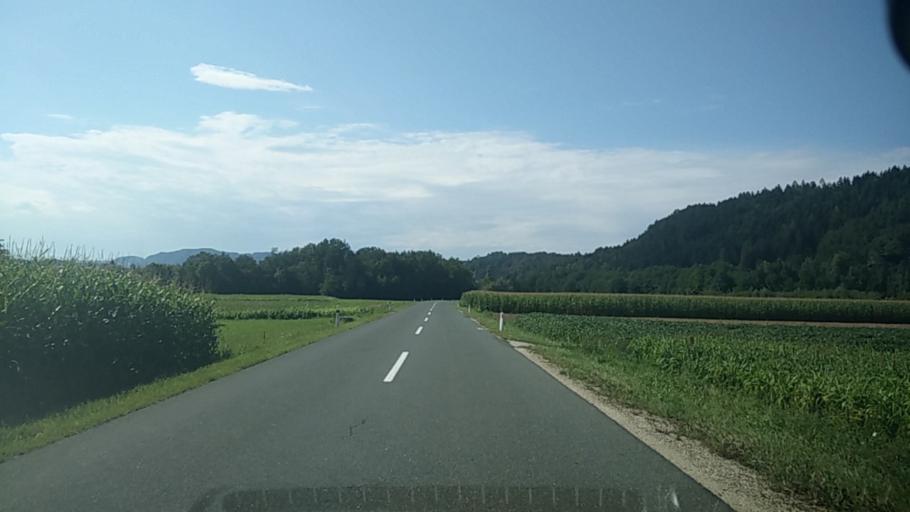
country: AT
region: Carinthia
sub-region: Politischer Bezirk Volkermarkt
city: Sittersdorf
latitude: 46.5522
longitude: 14.5802
